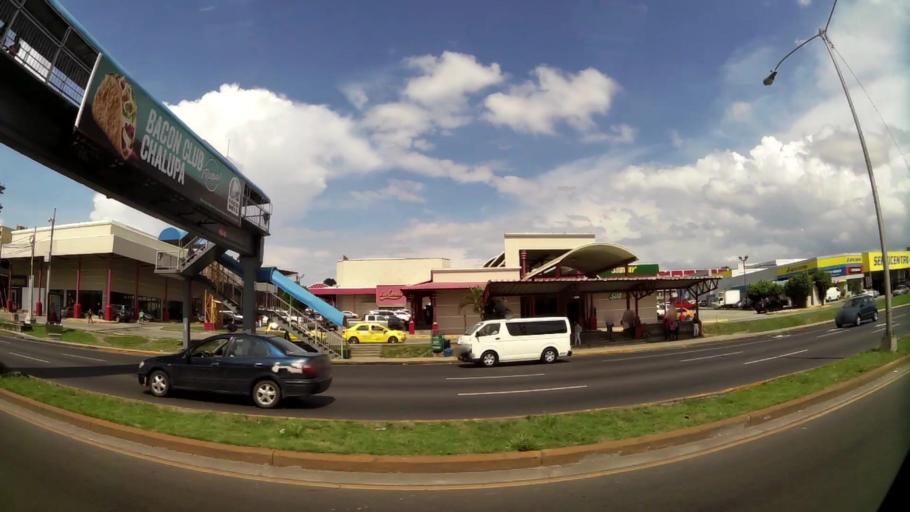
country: PA
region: Panama
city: San Miguelito
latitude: 9.0378
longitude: -79.4803
